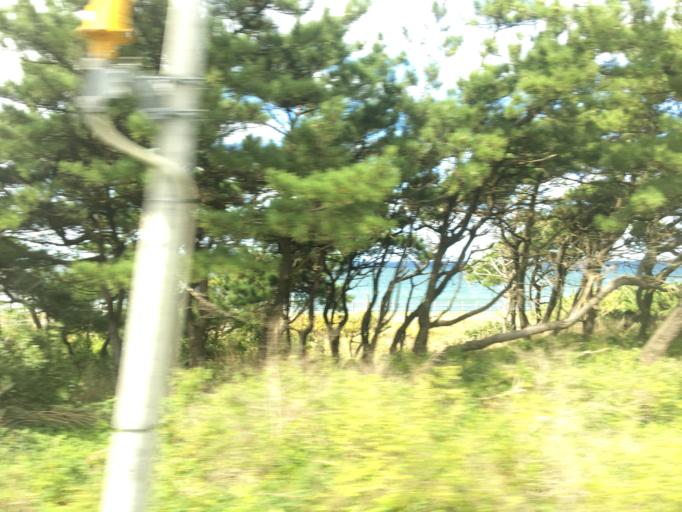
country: JP
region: Aomori
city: Shimokizukuri
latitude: 40.7653
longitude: 140.1658
